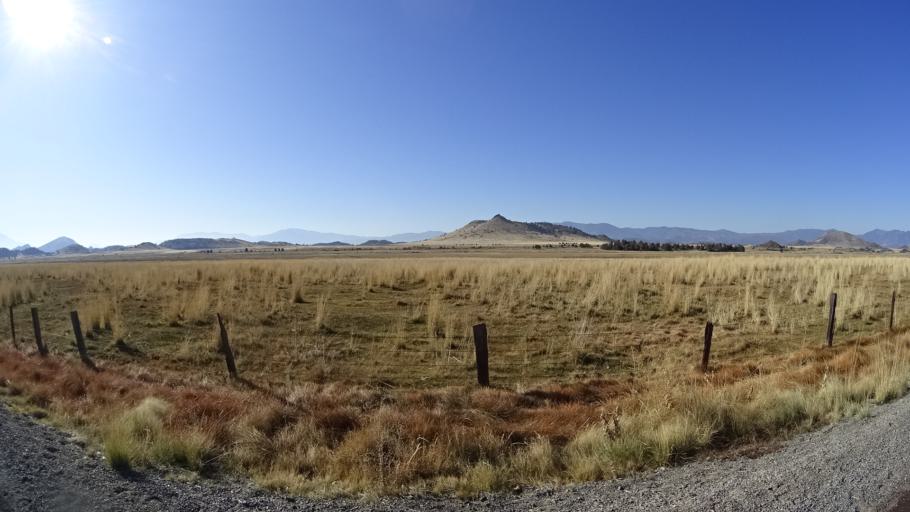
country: US
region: California
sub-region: Siskiyou County
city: Montague
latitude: 41.7169
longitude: -122.4458
